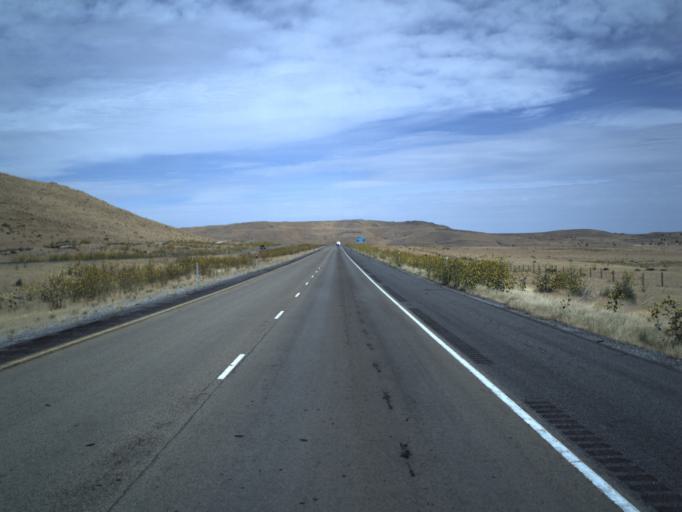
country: US
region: Utah
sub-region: Tooele County
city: Grantsville
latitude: 40.8154
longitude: -112.8772
